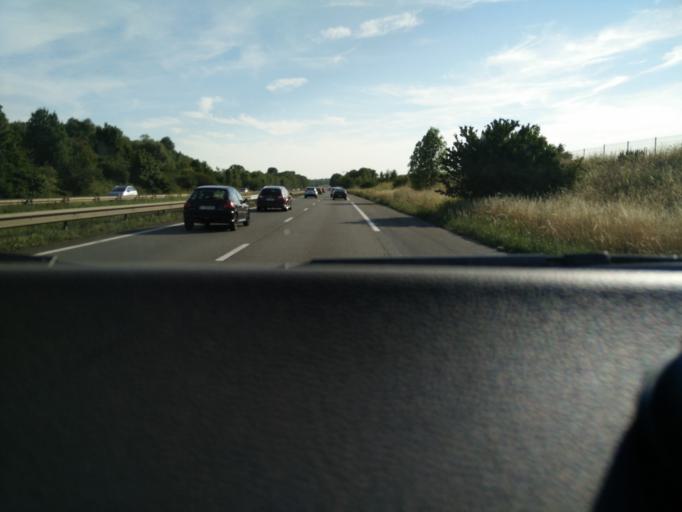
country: FR
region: Nord-Pas-de-Calais
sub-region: Departement du Nord
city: Prouvy
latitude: 50.3321
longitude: 3.4432
